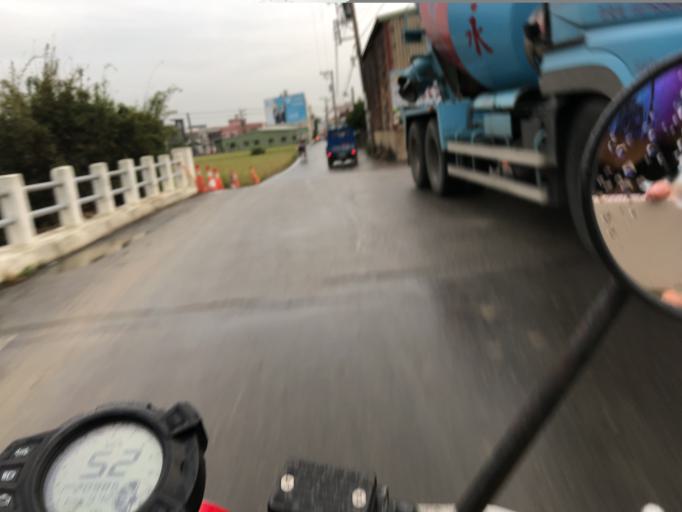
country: TW
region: Taiwan
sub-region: Hsinchu
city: Zhubei
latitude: 24.8429
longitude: 120.9862
